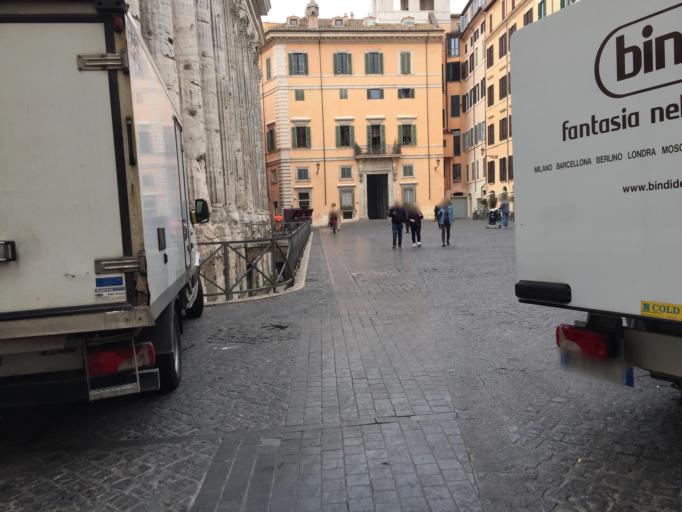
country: VA
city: Vatican City
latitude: 41.9002
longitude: 12.4798
